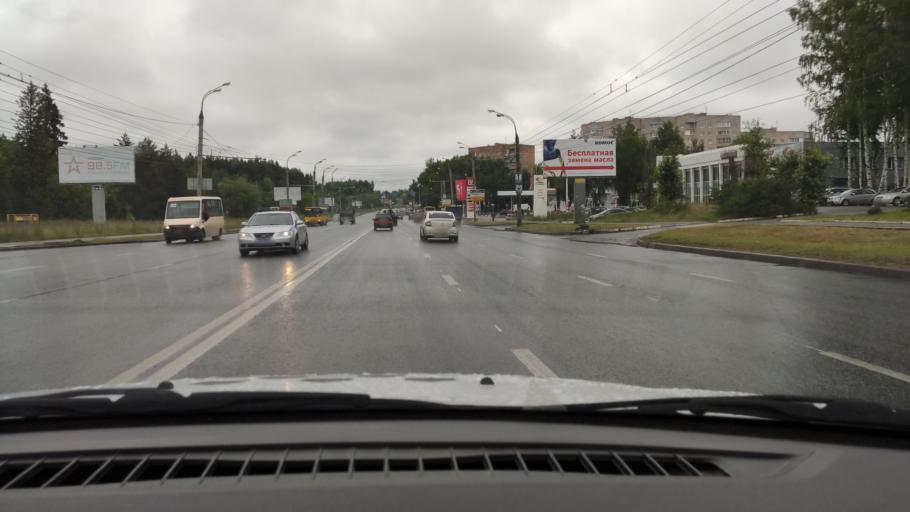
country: RU
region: Udmurtiya
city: Izhevsk
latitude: 56.8813
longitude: 53.2251
